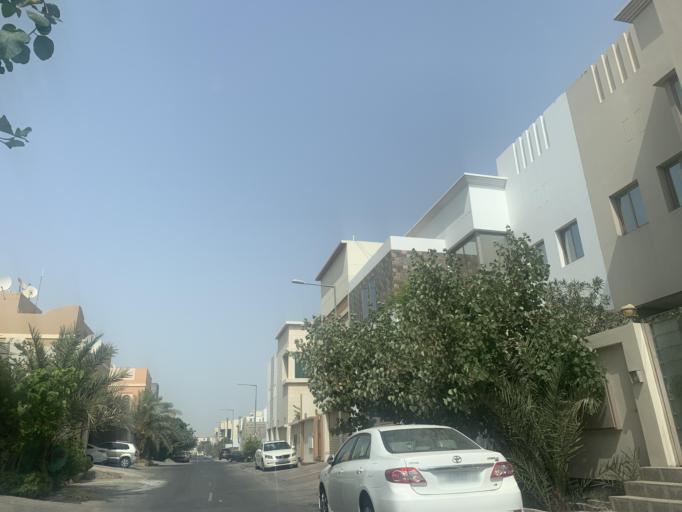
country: BH
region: Manama
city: Jidd Hafs
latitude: 26.2069
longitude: 50.4649
